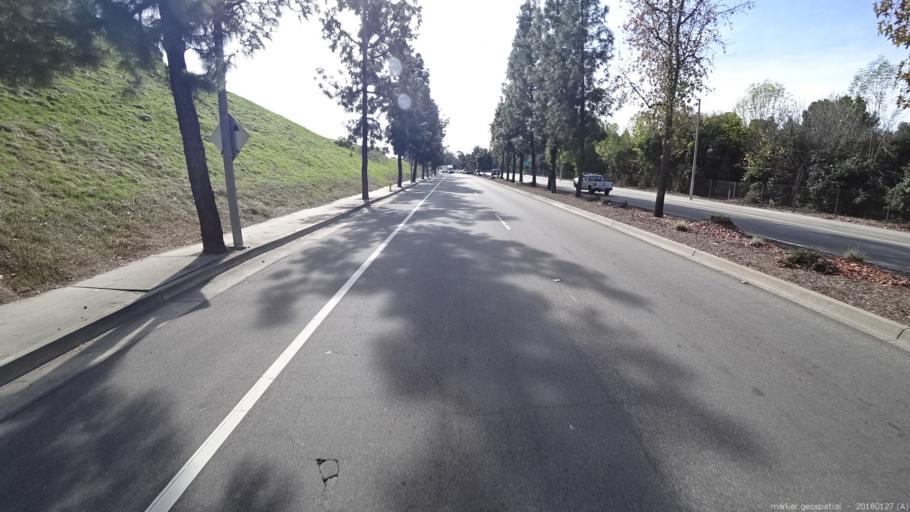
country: US
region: California
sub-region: Los Angeles County
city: Diamond Bar
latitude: 34.0272
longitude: -117.8112
